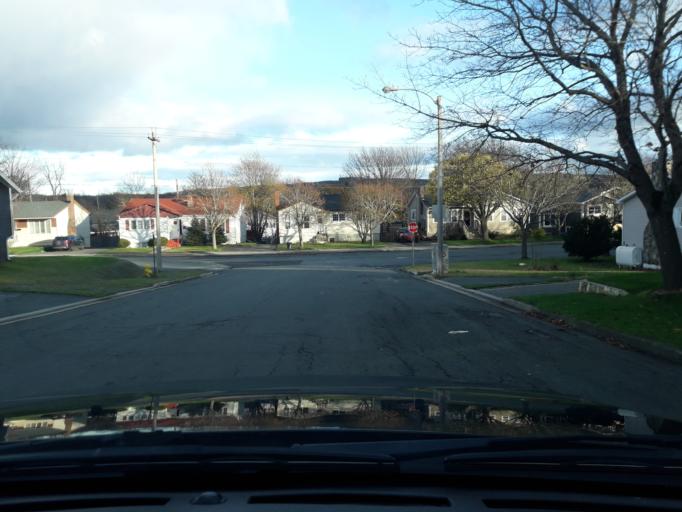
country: CA
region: Newfoundland and Labrador
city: St. John's
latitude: 47.5628
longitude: -52.7531
